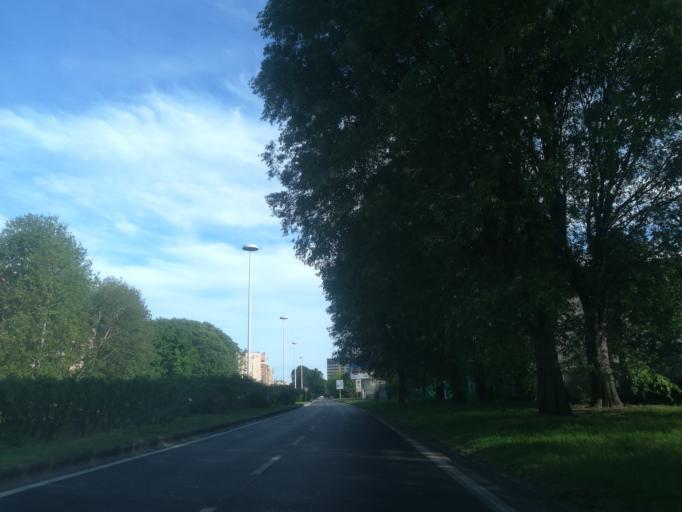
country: IT
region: Lombardy
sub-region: Citta metropolitana di Milano
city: Bresso
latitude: 45.5040
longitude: 9.1854
